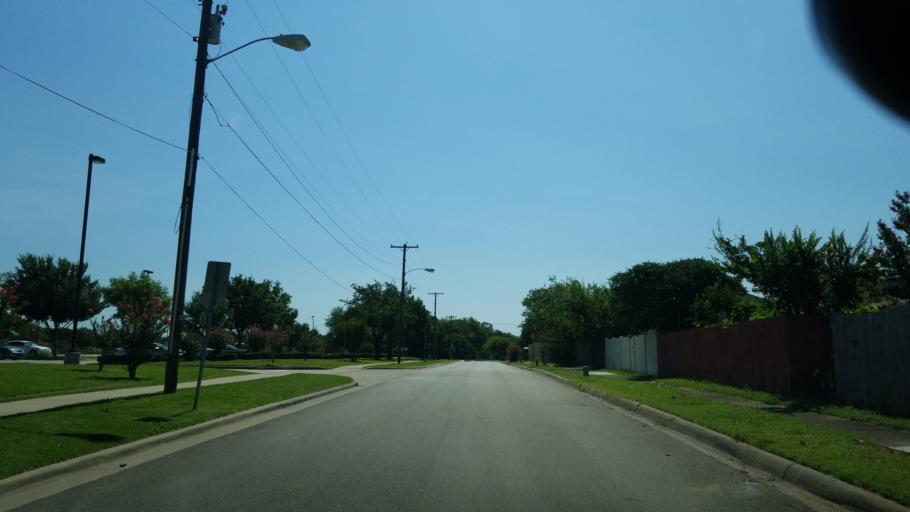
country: US
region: Texas
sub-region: Dallas County
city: Carrollton
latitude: 32.9699
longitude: -96.9093
